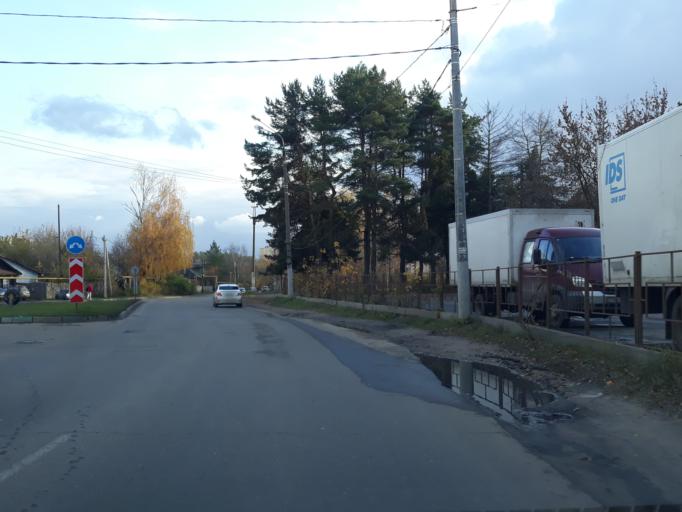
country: RU
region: Nizjnij Novgorod
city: Neklyudovo
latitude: 56.3387
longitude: 43.8666
